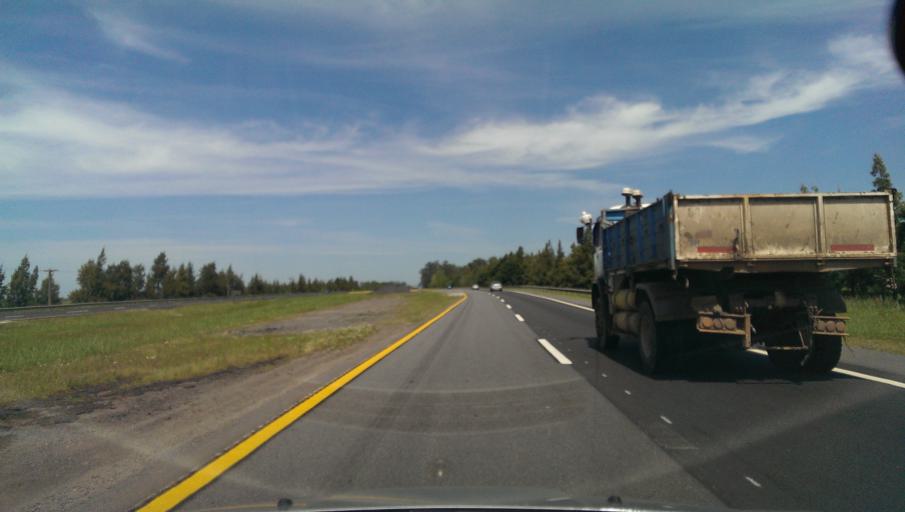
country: AR
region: Buenos Aires
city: San Miguel del Monte
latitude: -35.3249
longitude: -58.7877
